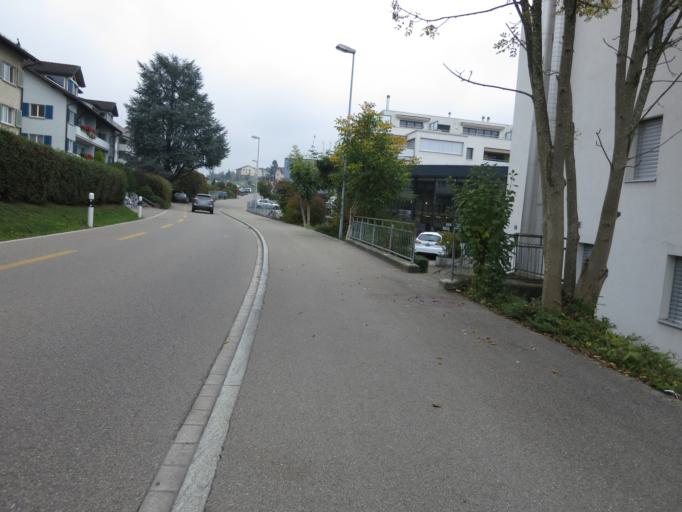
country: CH
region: Saint Gallen
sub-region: Wahlkreis See-Gaster
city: Rapperswil
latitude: 47.2398
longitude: 8.8242
